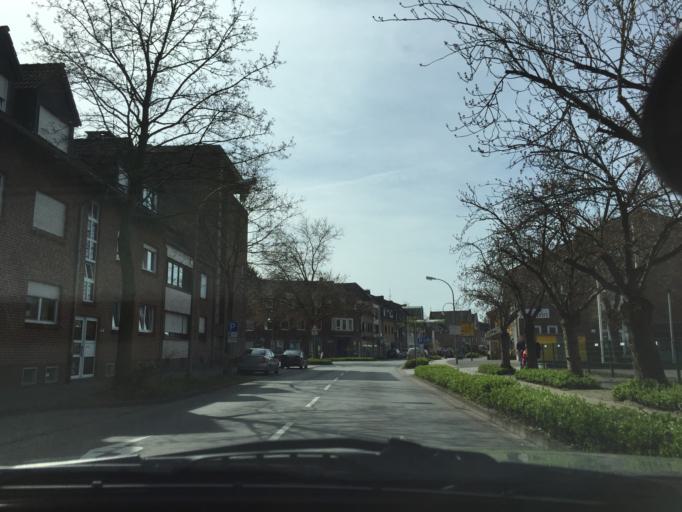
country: DE
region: North Rhine-Westphalia
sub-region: Regierungsbezirk Dusseldorf
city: Goch
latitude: 51.6809
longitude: 6.1595
